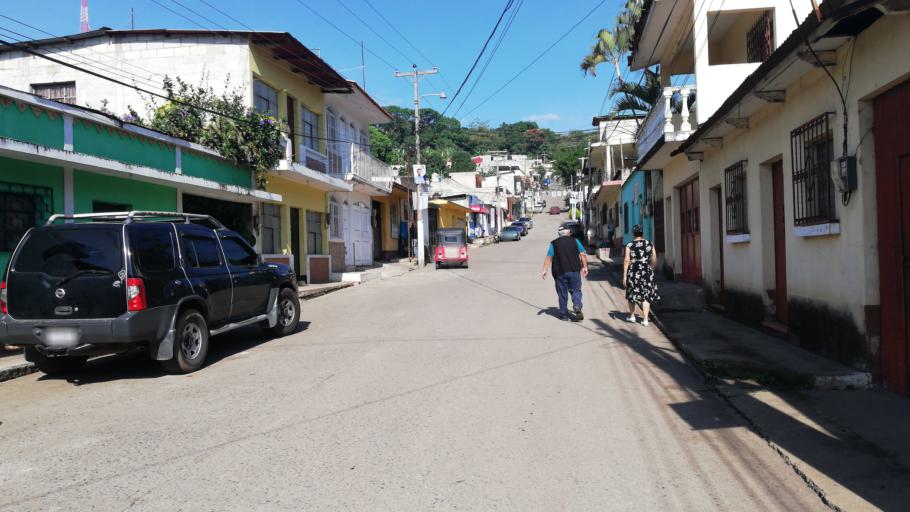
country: GT
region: Santa Rosa
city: Cuilapa
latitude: 14.2794
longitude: -90.3026
